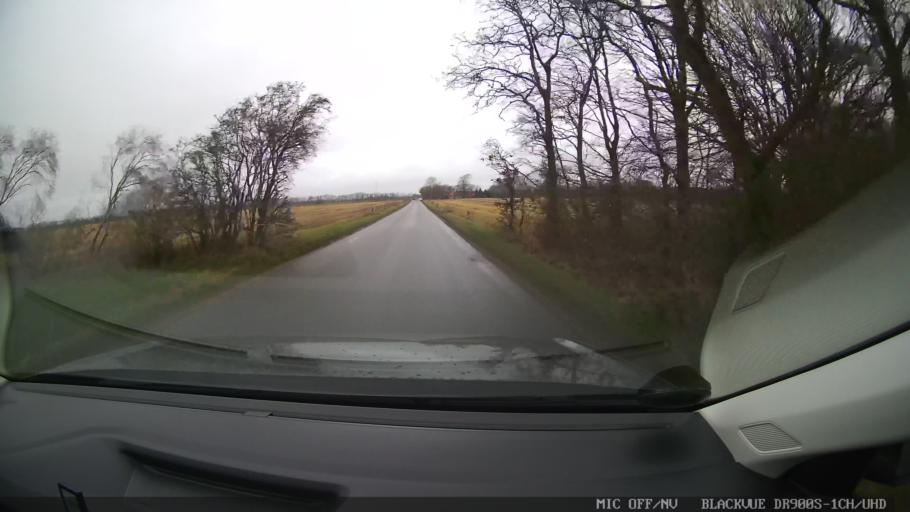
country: DK
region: Central Jutland
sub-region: Viborg Kommune
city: Karup
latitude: 56.3369
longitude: 9.2739
